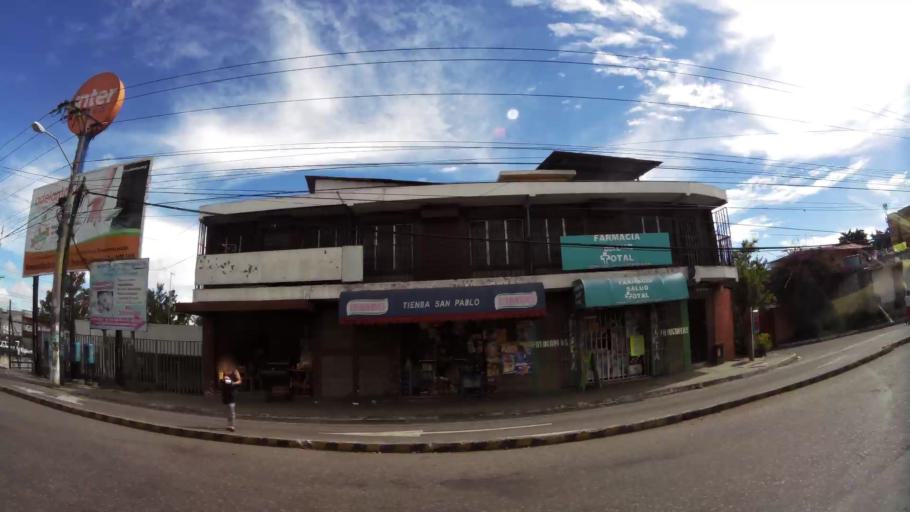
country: GT
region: Guatemala
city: Mixco
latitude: 14.6463
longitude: -90.5795
